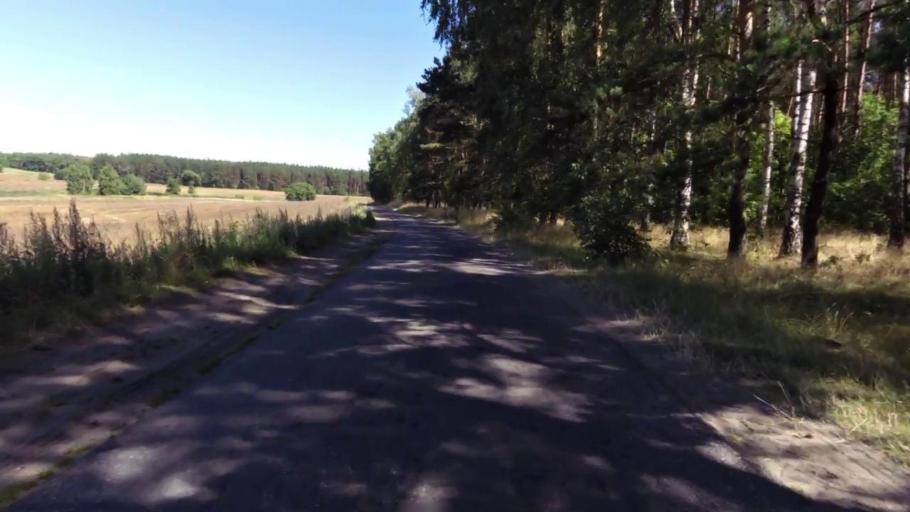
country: PL
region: West Pomeranian Voivodeship
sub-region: Powiat szczecinecki
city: Szczecinek
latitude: 53.6323
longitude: 16.6944
